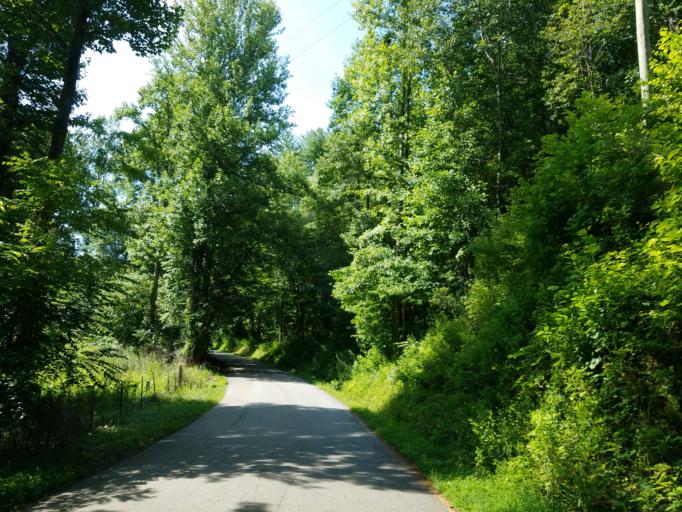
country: US
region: Georgia
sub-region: Dawson County
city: Dawsonville
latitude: 34.5655
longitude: -84.1465
